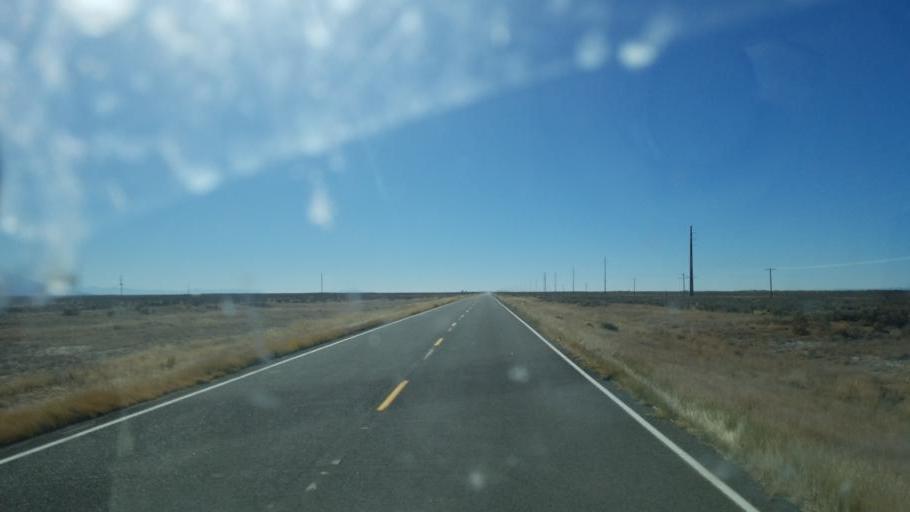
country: US
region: Colorado
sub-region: Saguache County
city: Center
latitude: 37.9225
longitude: -105.9000
